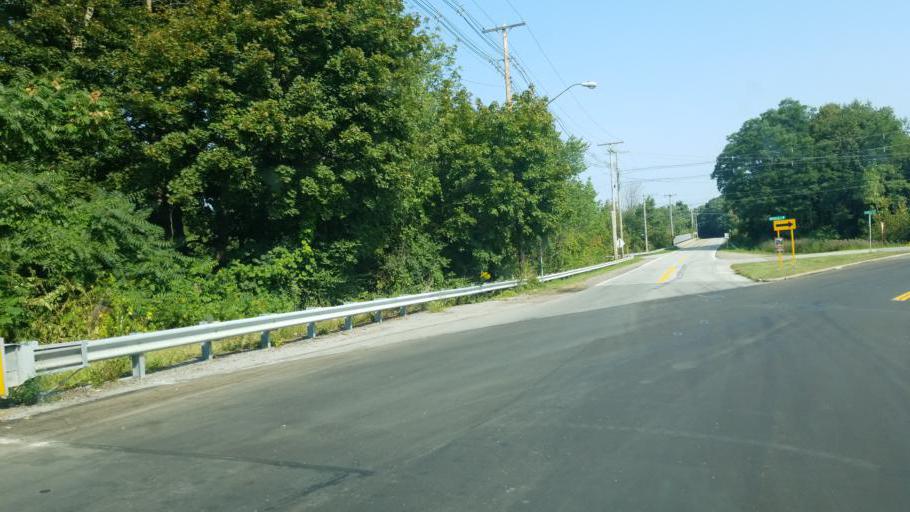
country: US
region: Ohio
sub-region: Lake County
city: Painesville
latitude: 41.7392
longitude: -81.2280
